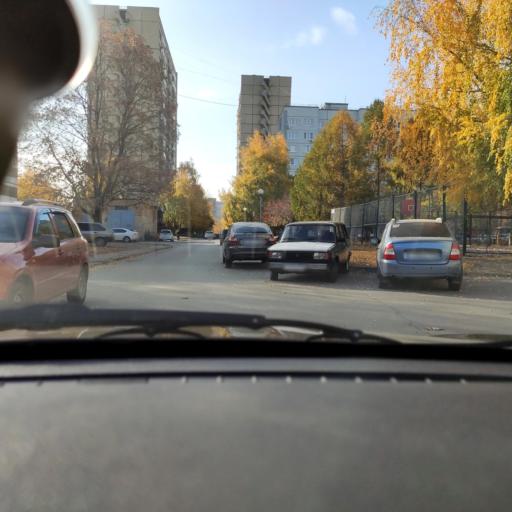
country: RU
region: Samara
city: Tol'yatti
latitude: 53.5279
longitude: 49.3290
